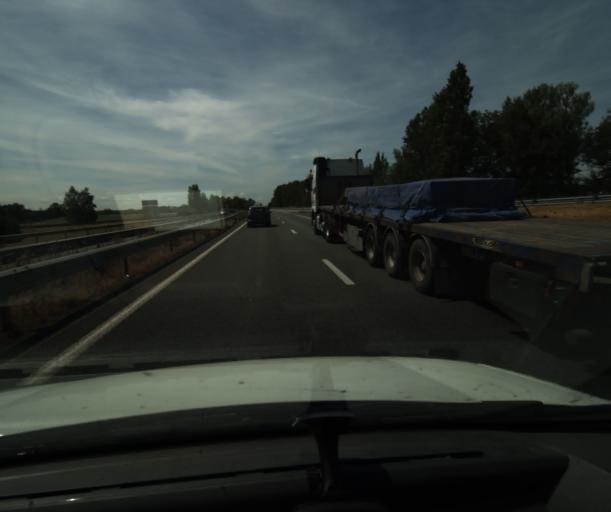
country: FR
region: Languedoc-Roussillon
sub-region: Departement de l'Aude
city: Bram
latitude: 43.2369
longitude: 2.0962
